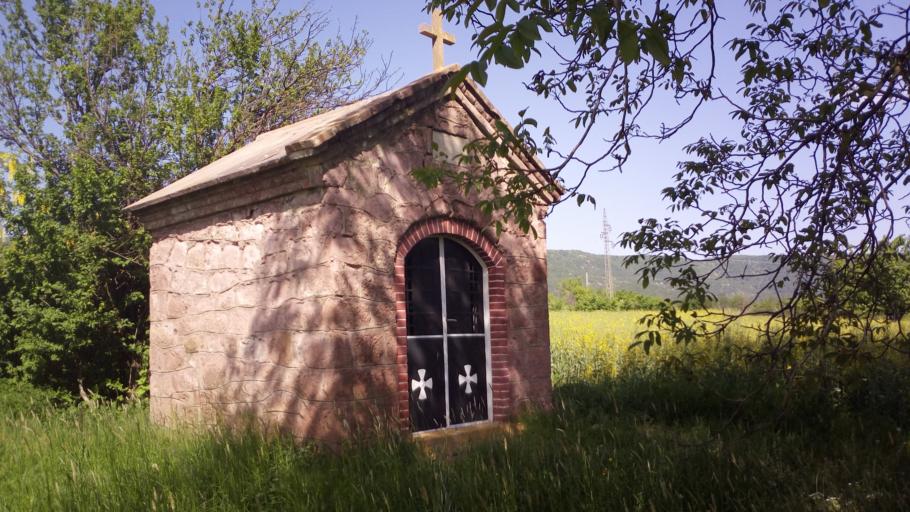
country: HU
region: Baranya
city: Pellerd
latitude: 46.0847
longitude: 18.1085
